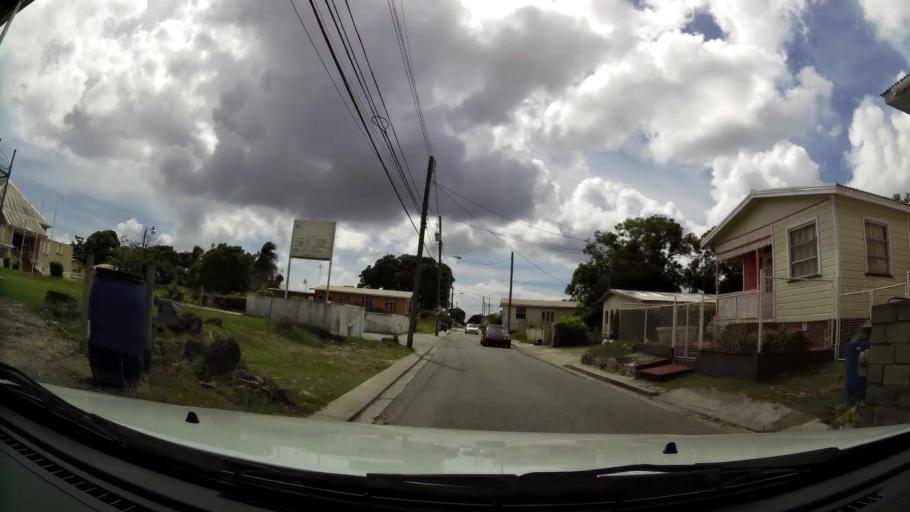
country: BB
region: Saint Michael
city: Bridgetown
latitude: 13.1200
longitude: -59.6182
